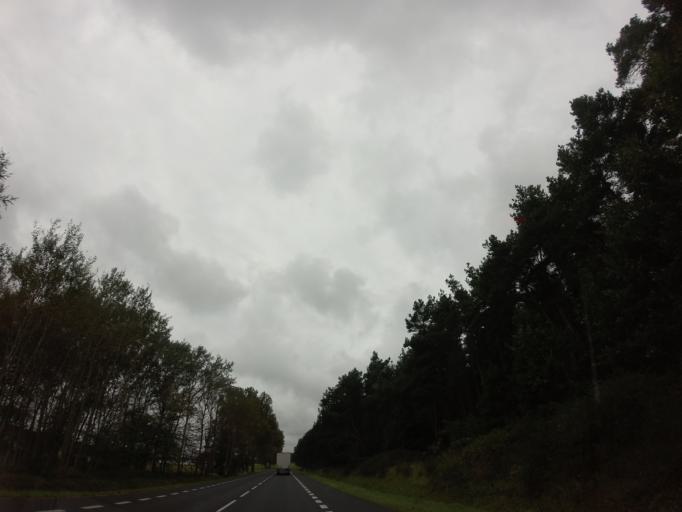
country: PL
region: West Pomeranian Voivodeship
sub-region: Powiat kamienski
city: Wolin
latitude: 53.8556
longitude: 14.5807
